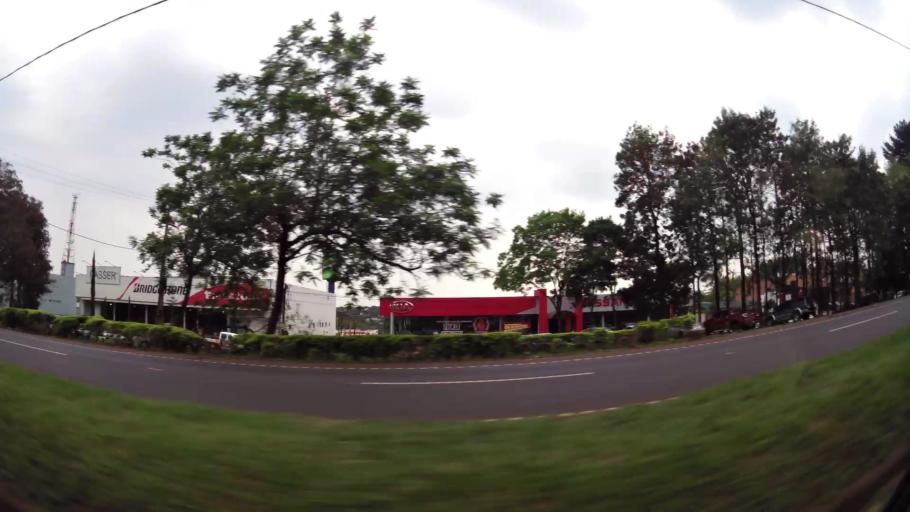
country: PY
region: Alto Parana
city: Ciudad del Este
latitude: -25.5005
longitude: -54.6582
